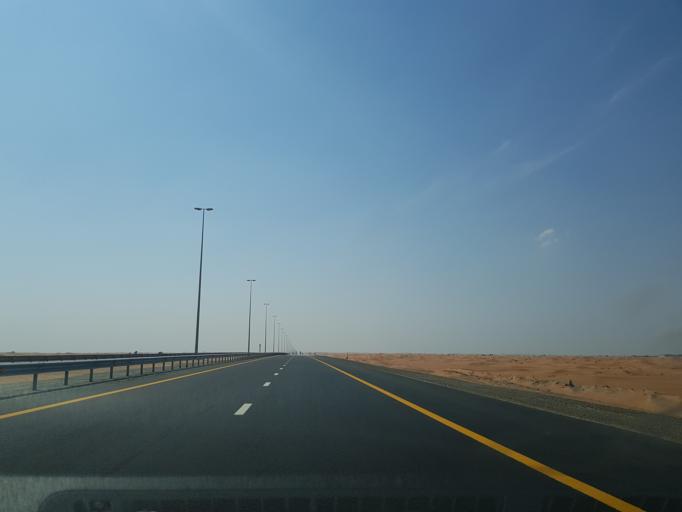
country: AE
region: Ash Shariqah
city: Adh Dhayd
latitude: 25.2530
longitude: 55.7615
